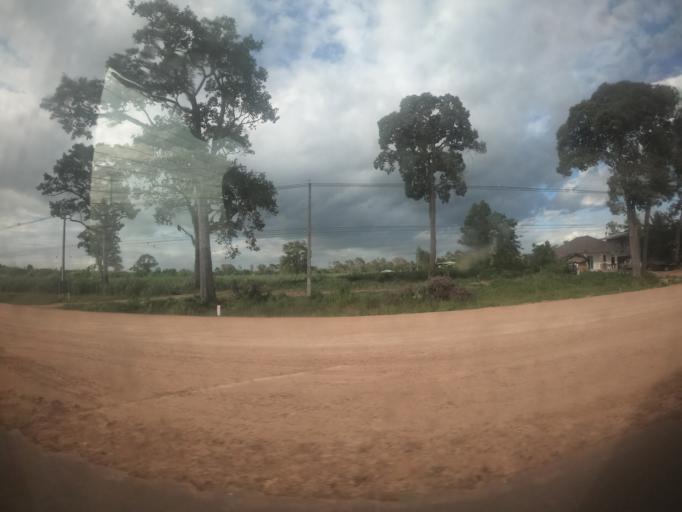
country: TH
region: Surin
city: Kap Choeng
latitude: 14.4927
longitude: 103.5719
